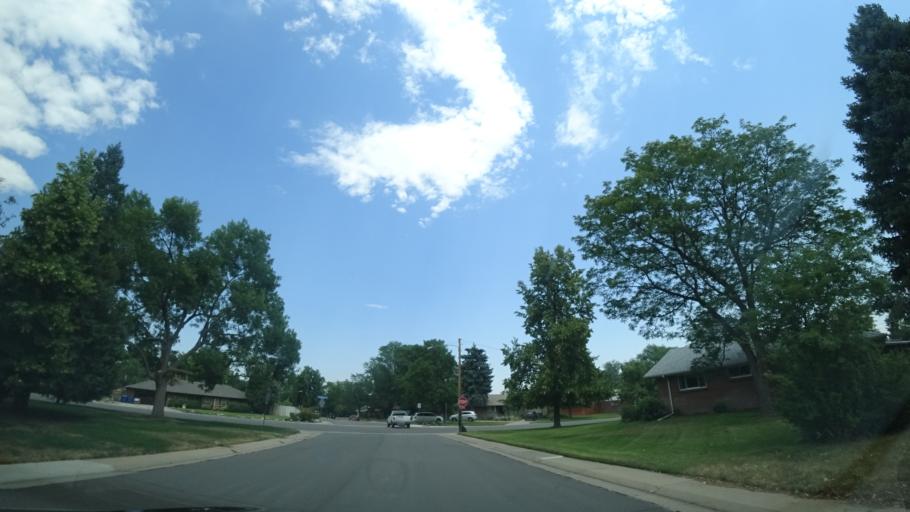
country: US
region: Colorado
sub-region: Jefferson County
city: Lakewood
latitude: 39.7229
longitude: -105.0968
